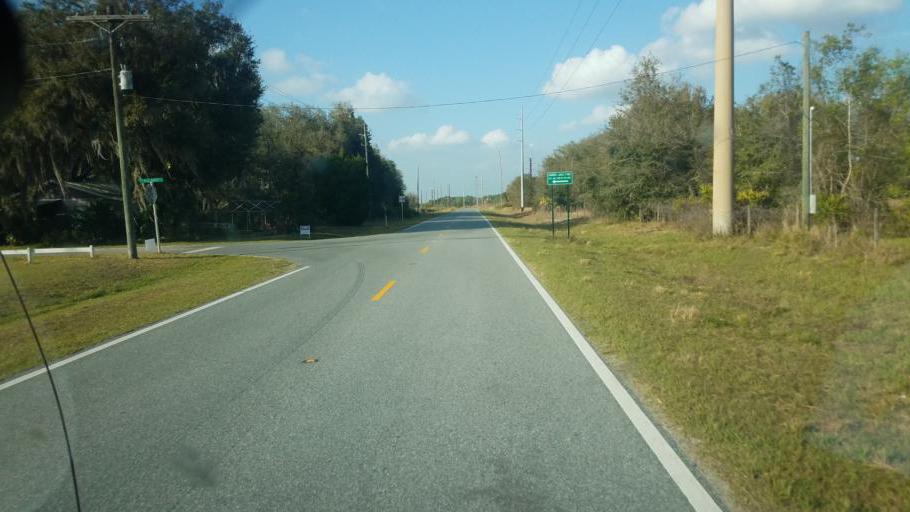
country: US
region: Florida
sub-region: Hardee County
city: Bowling Green
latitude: 27.6126
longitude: -81.9437
